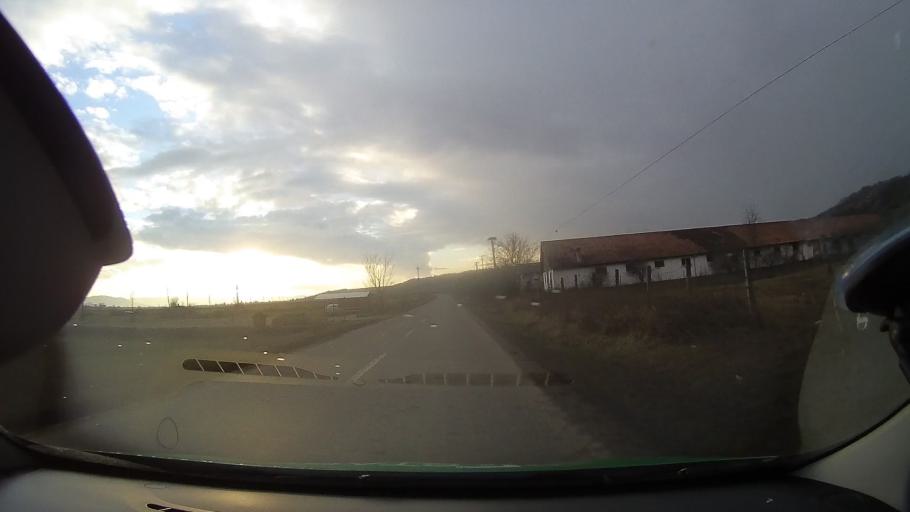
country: RO
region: Alba
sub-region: Comuna Lunca Muresului
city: Lunca Muresului
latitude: 46.4274
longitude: 23.8924
